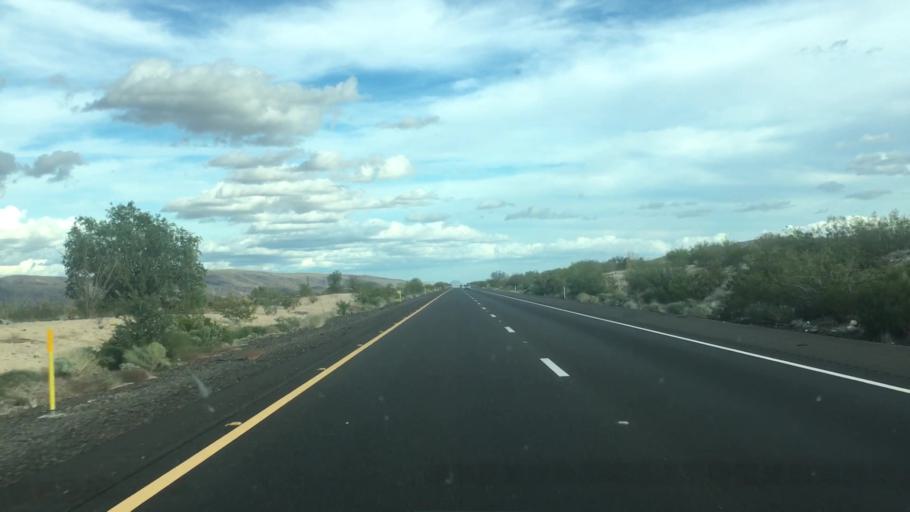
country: US
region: Arizona
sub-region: La Paz County
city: Quartzsite
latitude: 33.6579
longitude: -113.9872
